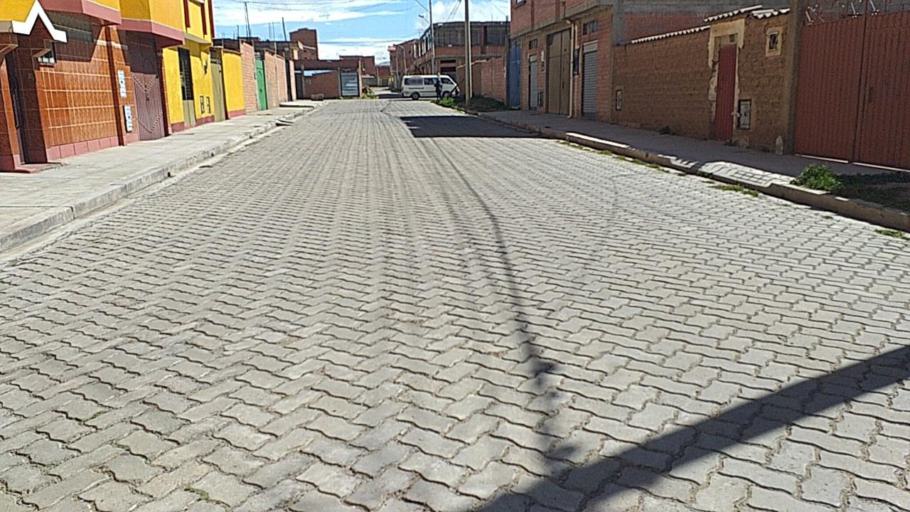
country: BO
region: La Paz
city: La Paz
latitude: -16.5182
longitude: -68.2017
